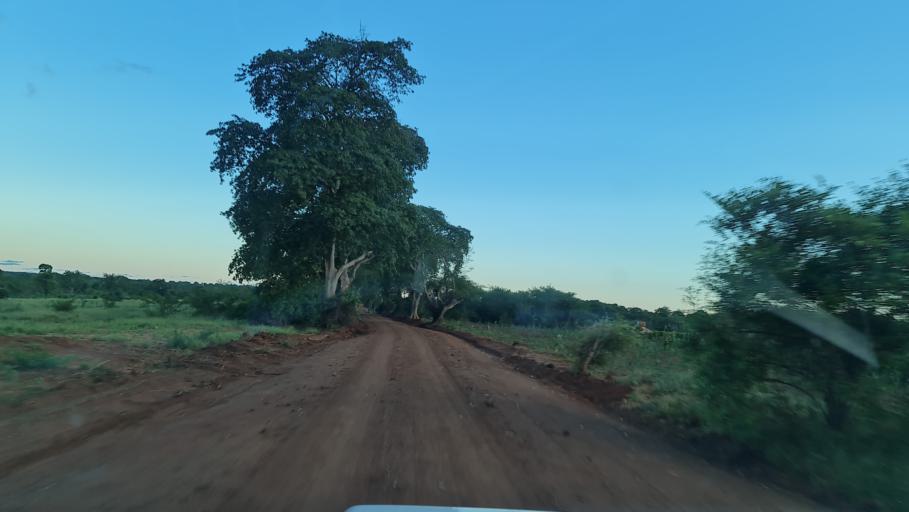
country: MZ
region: Nampula
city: Ilha de Mocambique
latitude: -14.9770
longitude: 40.0926
